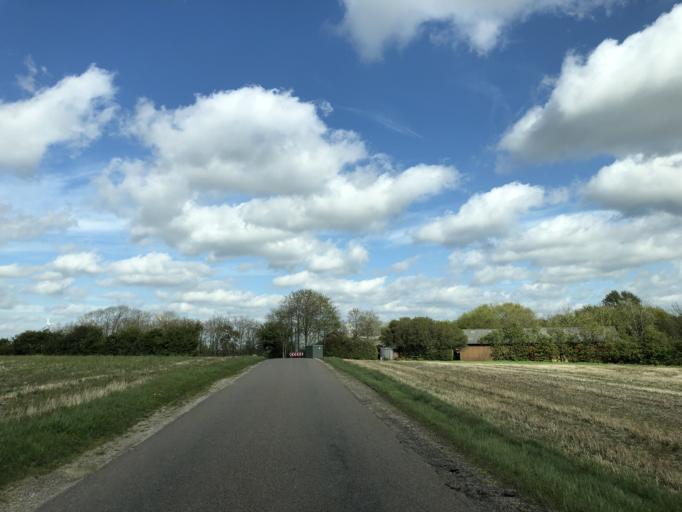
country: DK
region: Central Jutland
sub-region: Herning Kommune
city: Avlum
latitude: 56.3067
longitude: 8.7502
